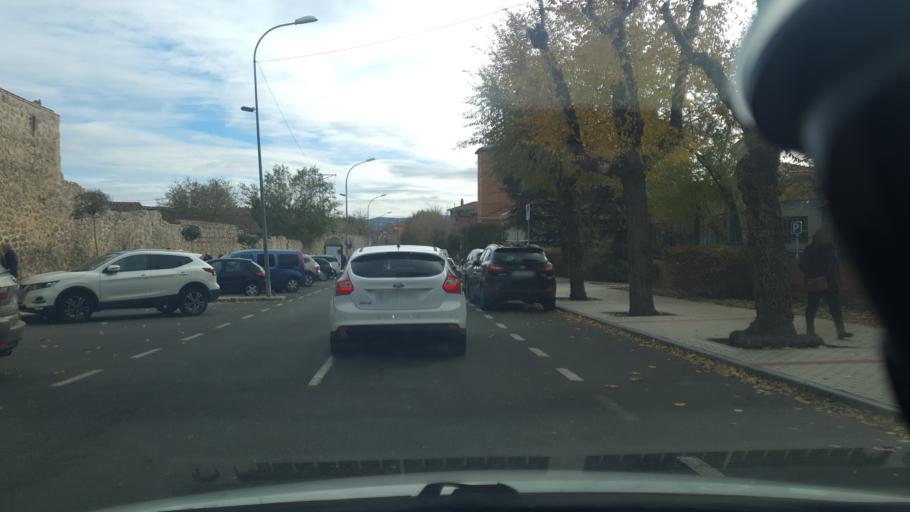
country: ES
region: Castille and Leon
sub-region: Provincia de Avila
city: Avila
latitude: 40.6496
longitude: -4.6892
